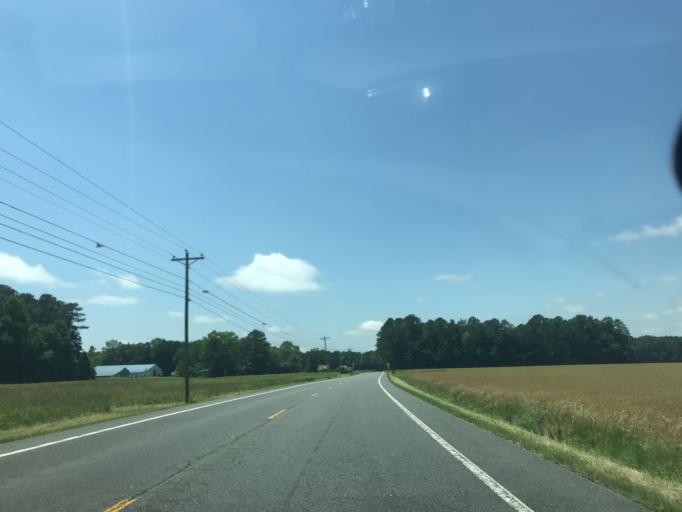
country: US
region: Maryland
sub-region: Caroline County
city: Federalsburg
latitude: 38.6328
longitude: -75.7769
